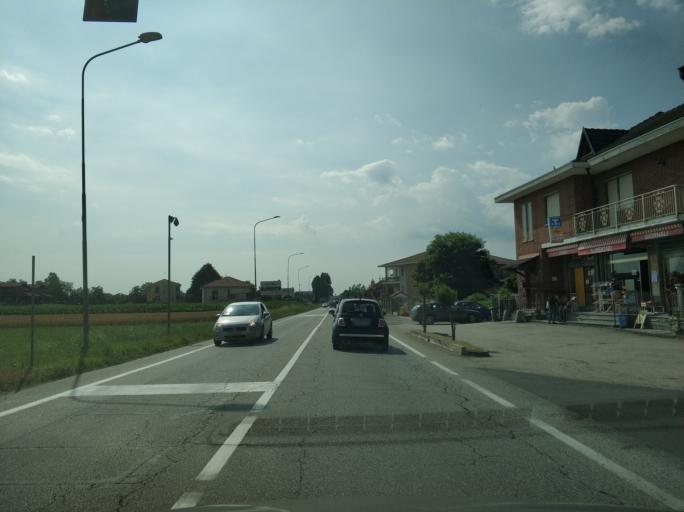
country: IT
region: Piedmont
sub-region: Provincia di Torino
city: Marocchi
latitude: 44.9430
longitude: 7.8150
